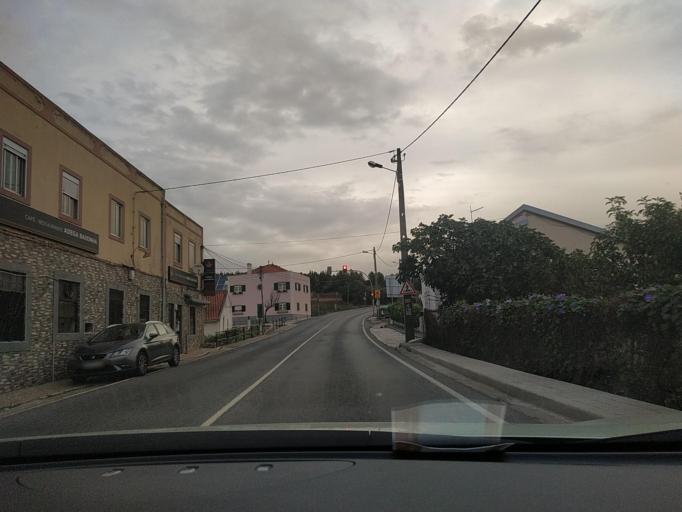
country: PT
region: Lisbon
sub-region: Loures
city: Loures
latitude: 38.8491
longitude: -9.1608
